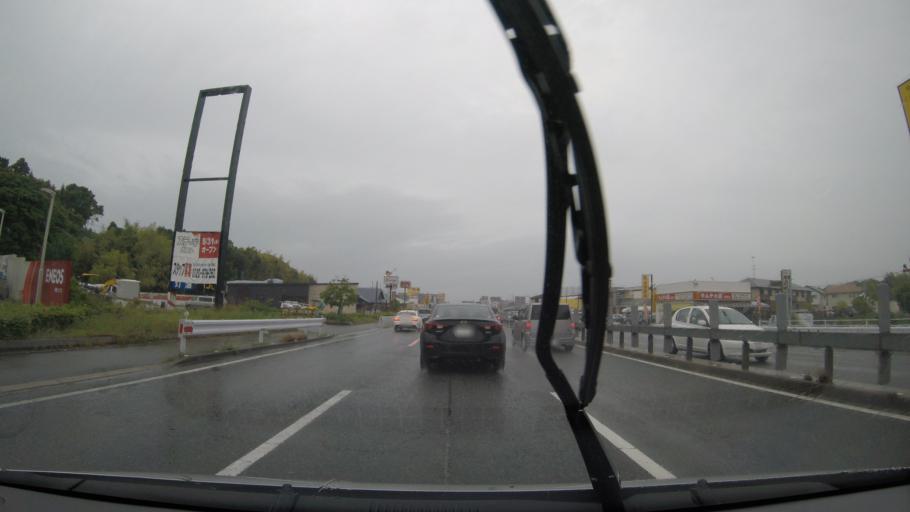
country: JP
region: Fukuoka
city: Shingu
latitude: 33.6884
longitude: 130.4533
